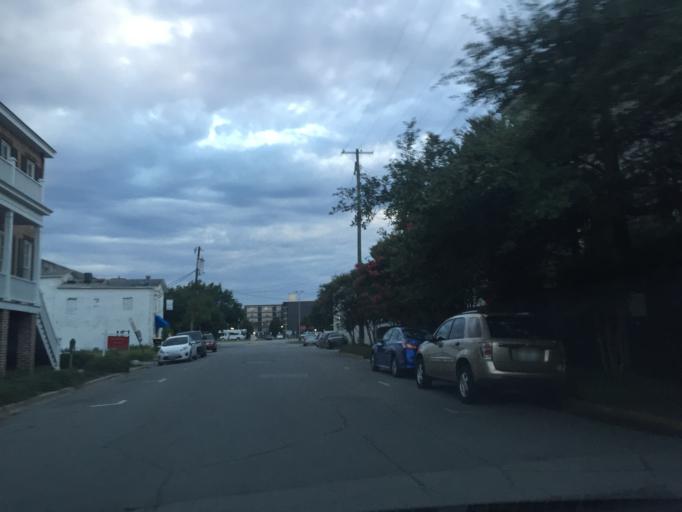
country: US
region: Georgia
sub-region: Chatham County
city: Savannah
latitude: 32.0746
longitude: -81.0969
